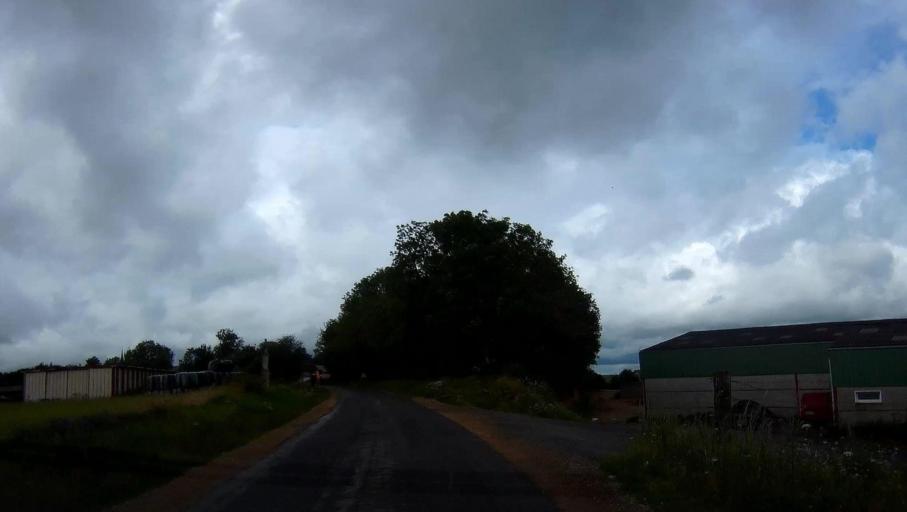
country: FR
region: Champagne-Ardenne
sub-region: Departement des Ardennes
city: Rimogne
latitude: 49.7609
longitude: 4.5140
